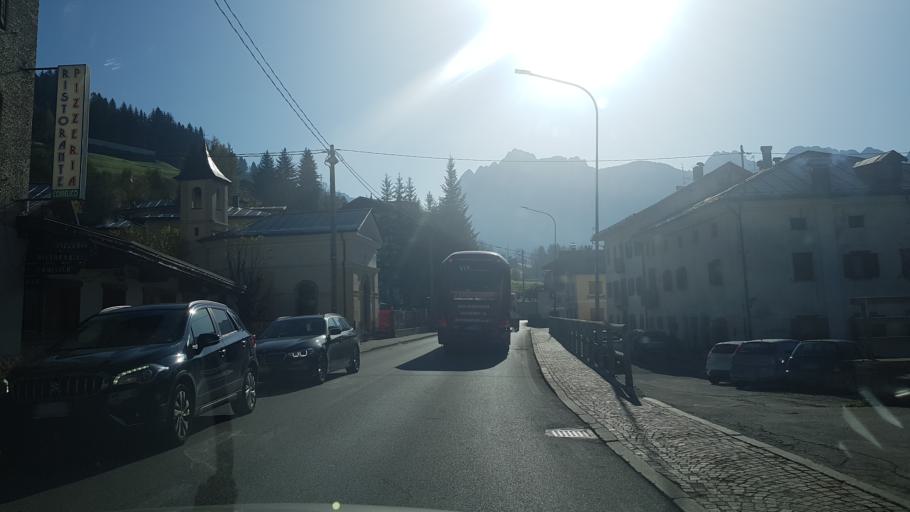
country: IT
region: Veneto
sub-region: Provincia di Belluno
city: San Nicolo Comelico
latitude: 46.5768
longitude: 12.5319
